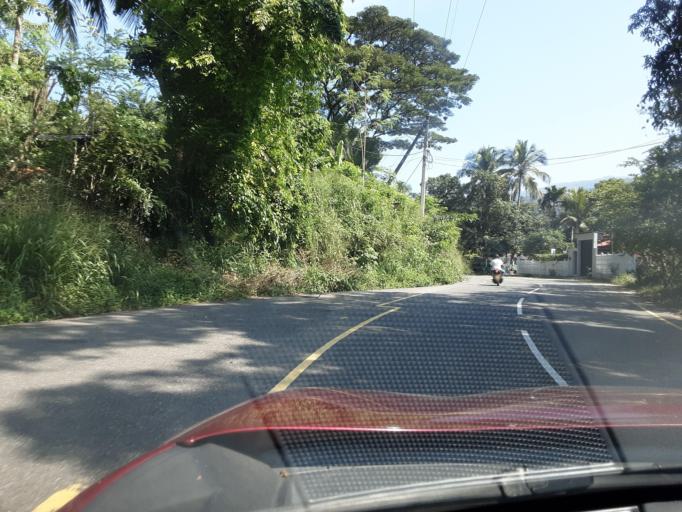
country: LK
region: Uva
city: Badulla
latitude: 7.0379
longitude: 81.0595
